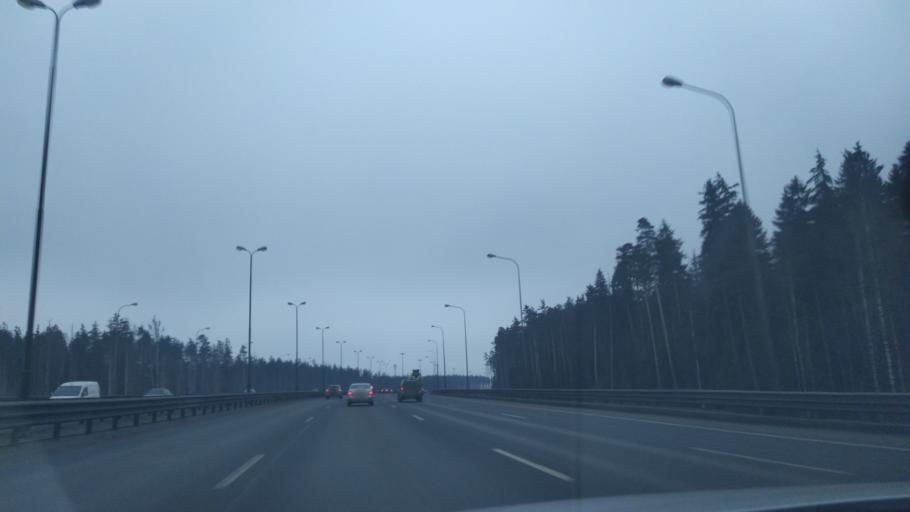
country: RU
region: Leningrad
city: Yanino Vtoroye
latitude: 59.9673
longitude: 30.5525
